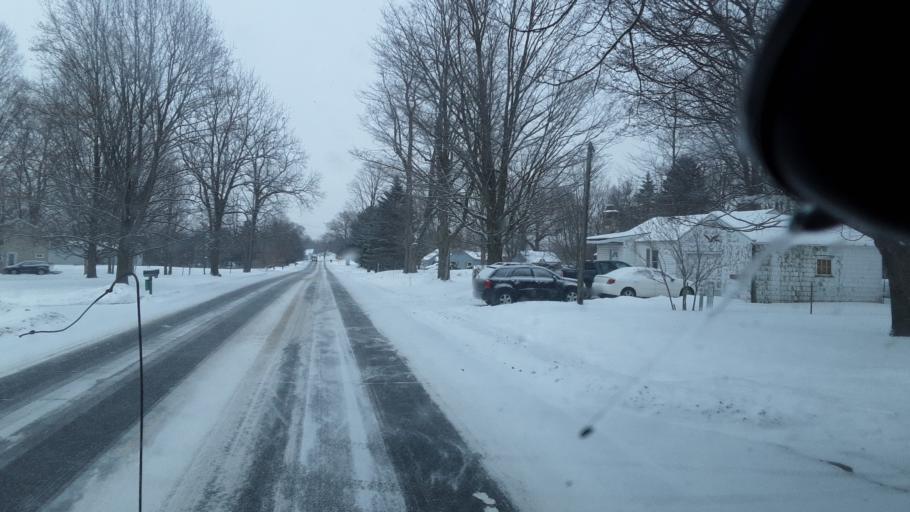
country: US
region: Michigan
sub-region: Ingham County
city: Mason
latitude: 42.5430
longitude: -84.3612
